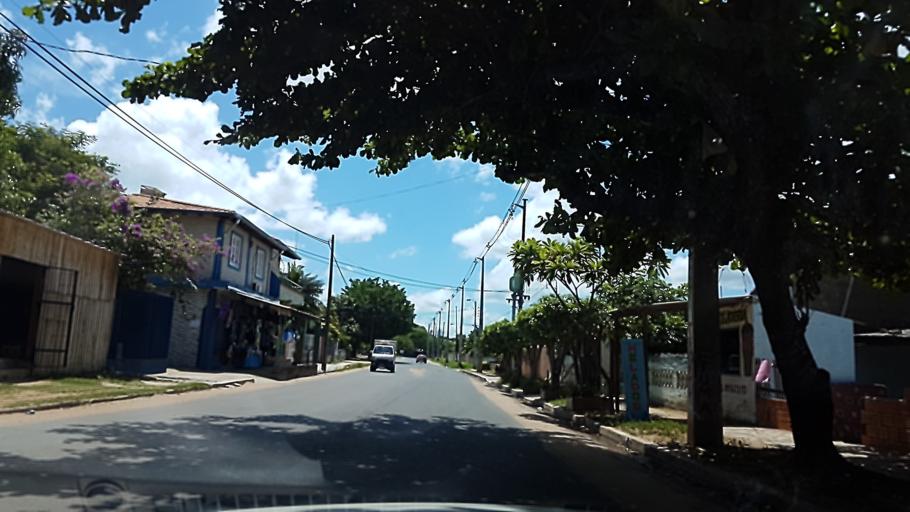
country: PY
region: Central
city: Colonia Mariano Roque Alonso
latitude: -25.2447
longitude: -57.5314
